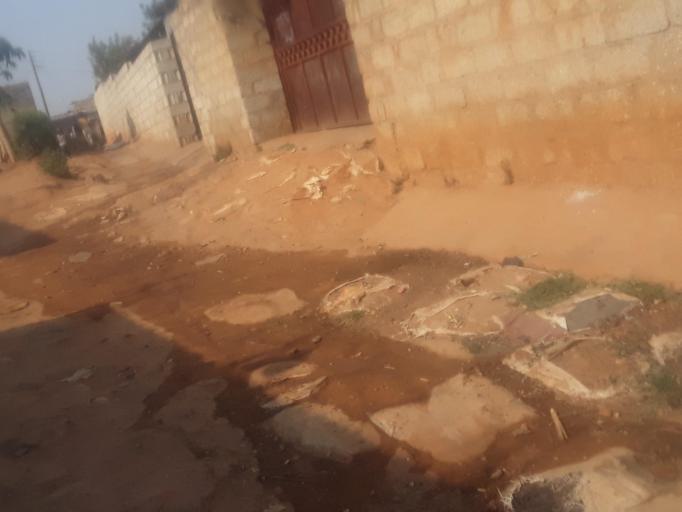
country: ZM
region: Lusaka
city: Lusaka
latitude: -15.3591
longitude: 28.2944
